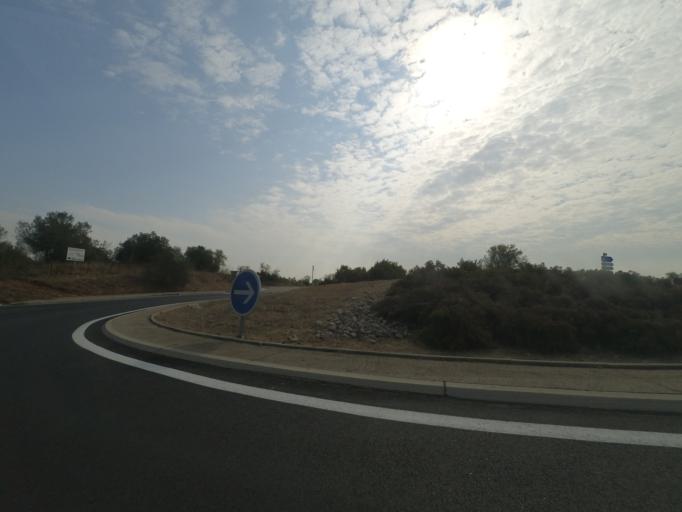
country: FR
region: Languedoc-Roussillon
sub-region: Departement de l'Herault
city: Saint-Christol
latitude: 43.7312
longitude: 4.0980
